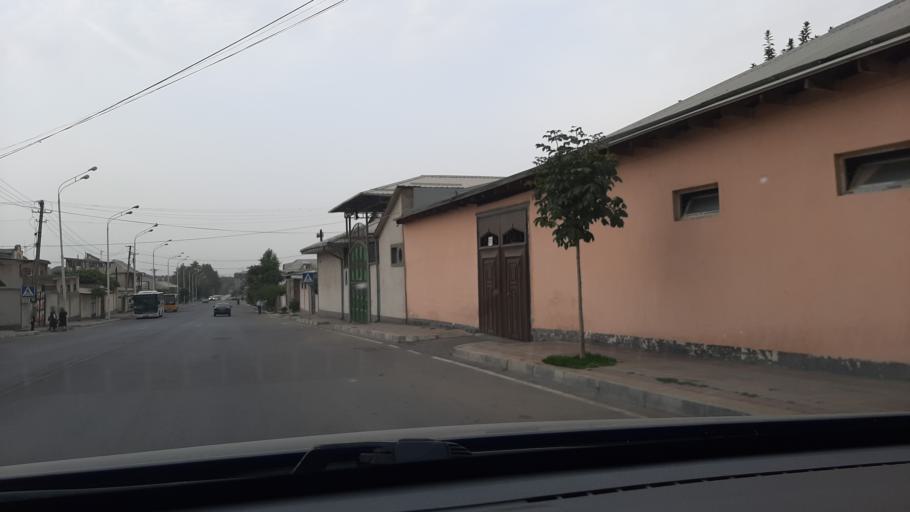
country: TJ
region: Dushanbe
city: Dushanbe
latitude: 38.6123
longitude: 68.7826
